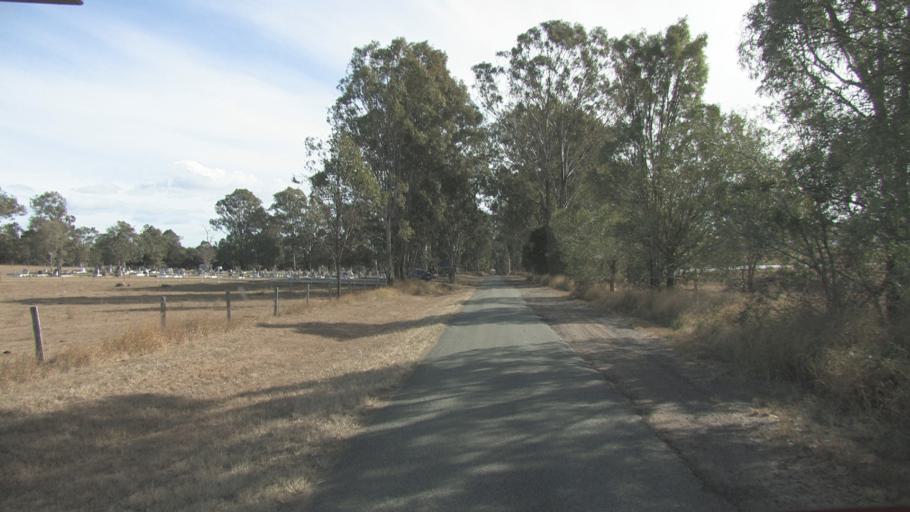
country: AU
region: Queensland
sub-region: Logan
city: Cedar Vale
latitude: -27.8941
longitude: 152.9713
